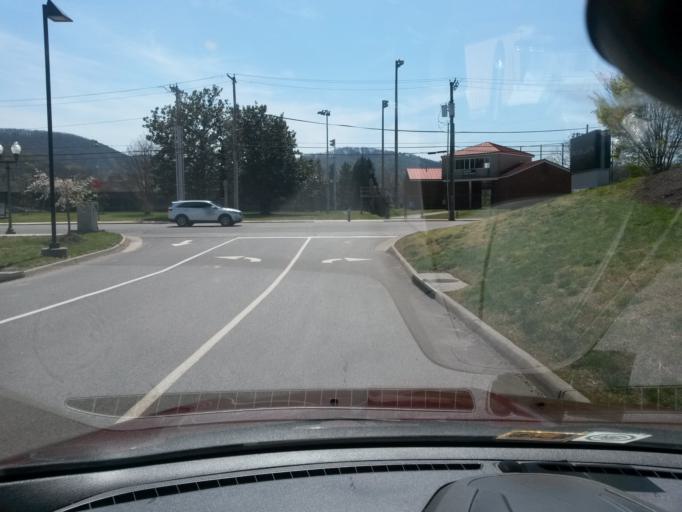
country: US
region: Virginia
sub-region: City of Roanoke
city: Cedar Bluff
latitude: 37.2561
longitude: -79.9465
